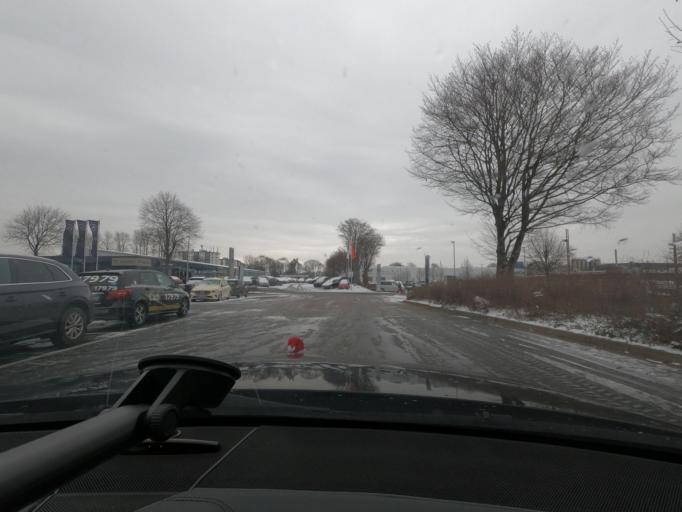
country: DE
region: Schleswig-Holstein
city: Flensburg
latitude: 54.7696
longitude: 9.4253
